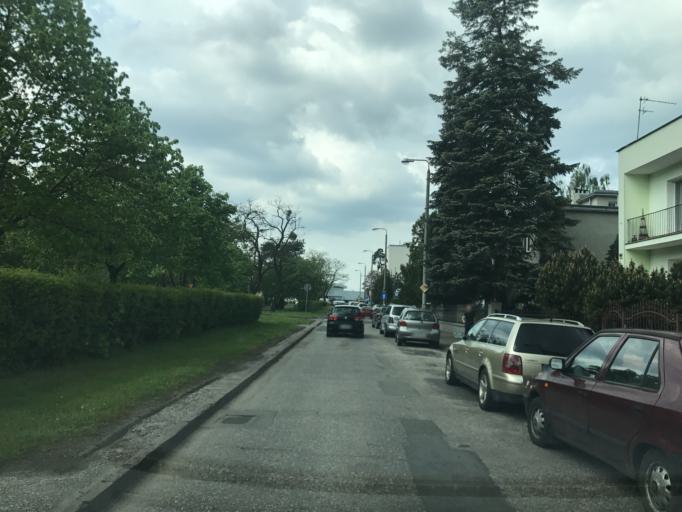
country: PL
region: Kujawsko-Pomorskie
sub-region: Bydgoszcz
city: Bydgoszcz
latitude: 53.1425
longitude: 18.0241
